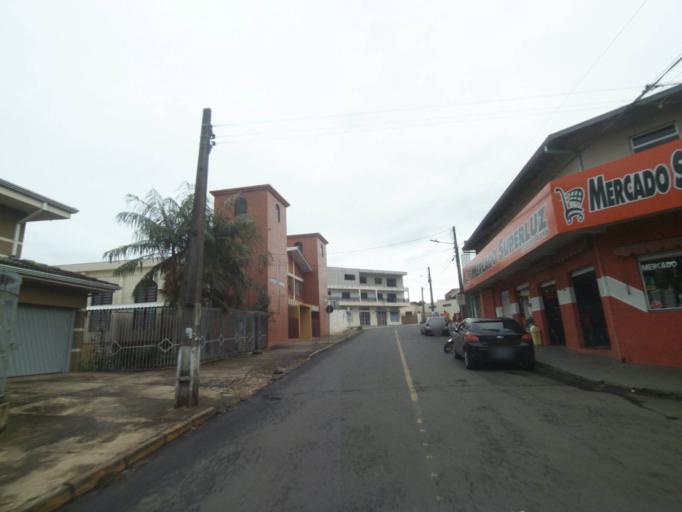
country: BR
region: Parana
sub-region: Telemaco Borba
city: Telemaco Borba
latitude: -24.3257
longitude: -50.6423
